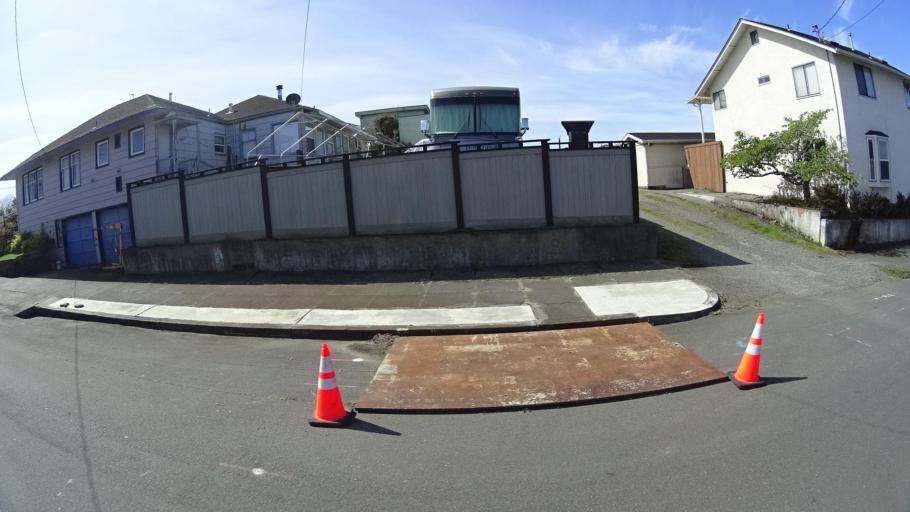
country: US
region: California
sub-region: Humboldt County
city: Eureka
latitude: 40.7905
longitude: -124.1661
